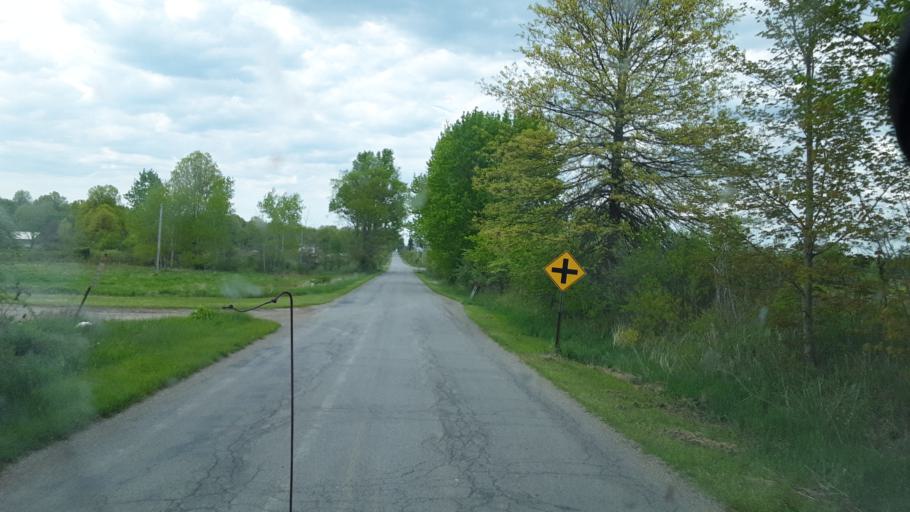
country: US
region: Ohio
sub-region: Portage County
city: Windham
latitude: 41.2920
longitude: -80.9835
